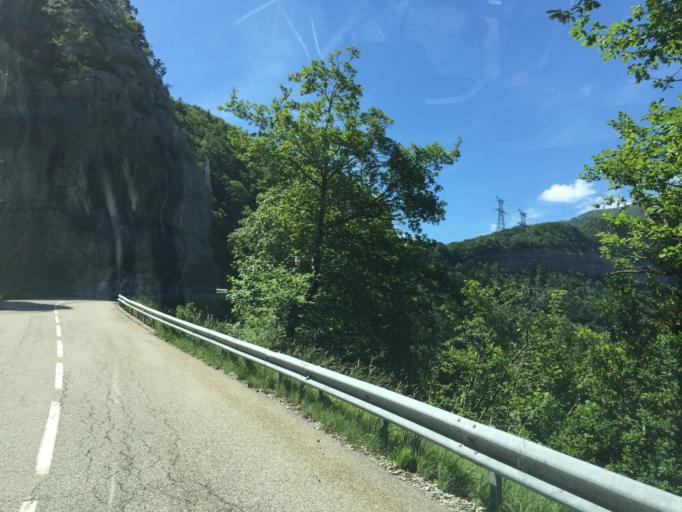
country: FR
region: Rhone-Alpes
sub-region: Departement de la Savoie
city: Saint-Baldoph
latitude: 45.5187
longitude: 5.9265
